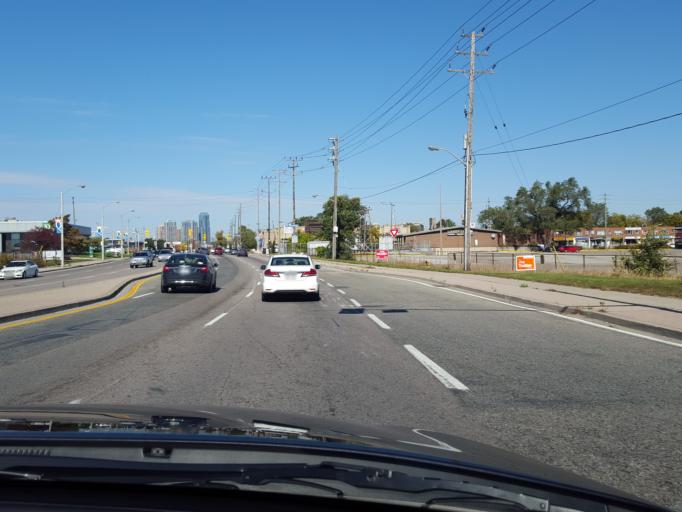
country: CA
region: Ontario
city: Etobicoke
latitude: 43.6193
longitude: -79.5261
